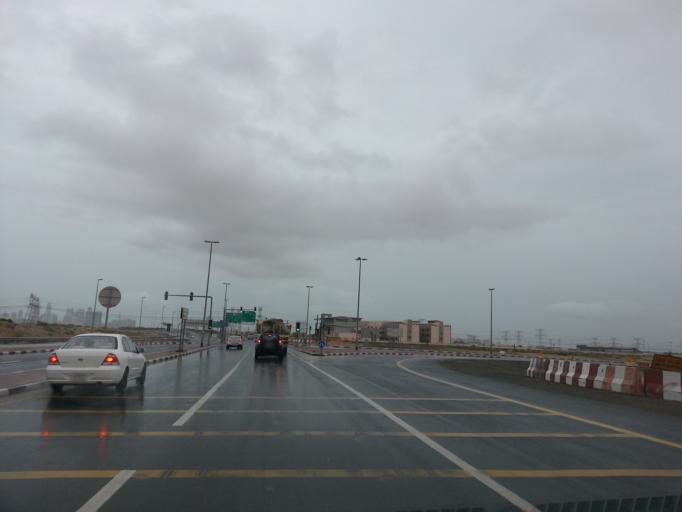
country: AE
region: Dubai
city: Dubai
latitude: 25.0705
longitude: 55.2174
